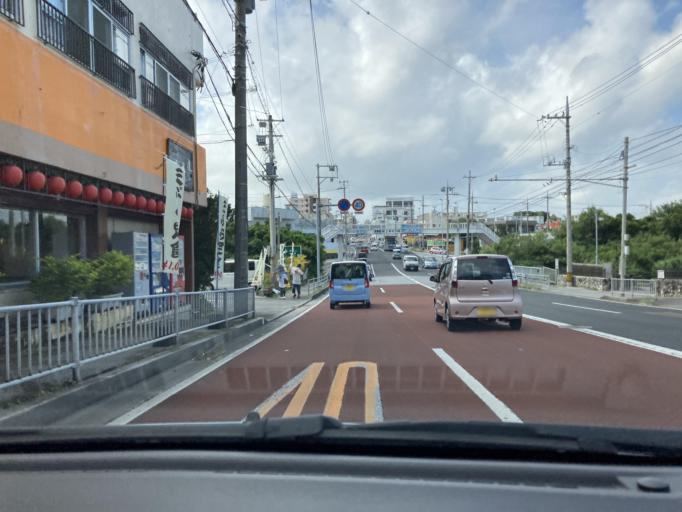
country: JP
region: Okinawa
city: Ginowan
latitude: 26.2590
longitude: 127.7420
